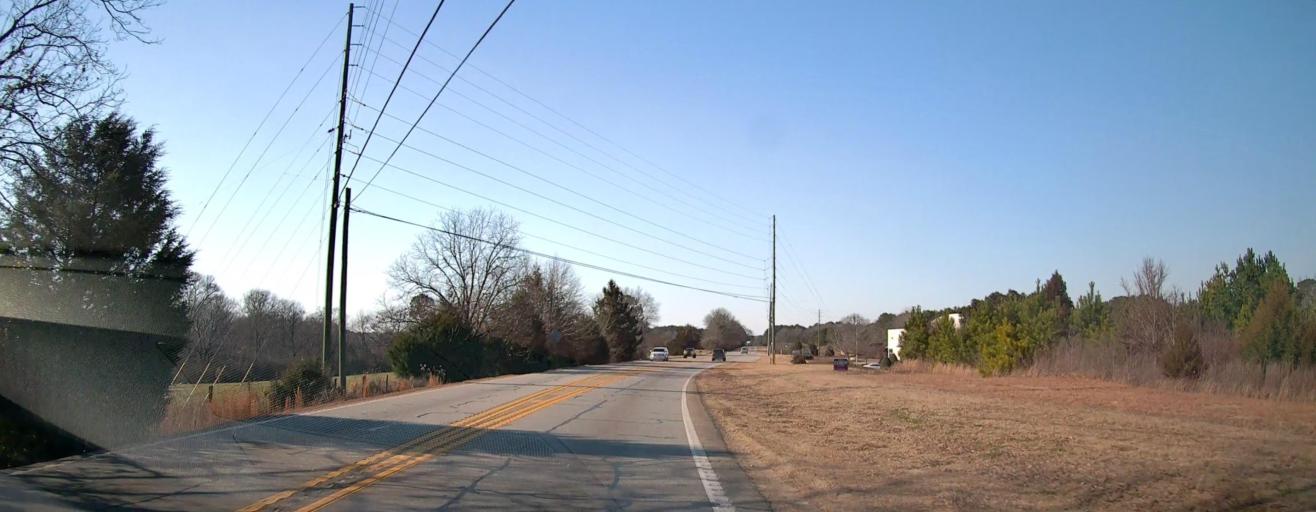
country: US
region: Georgia
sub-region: Henry County
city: Locust Grove
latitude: 33.3216
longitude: -84.0602
